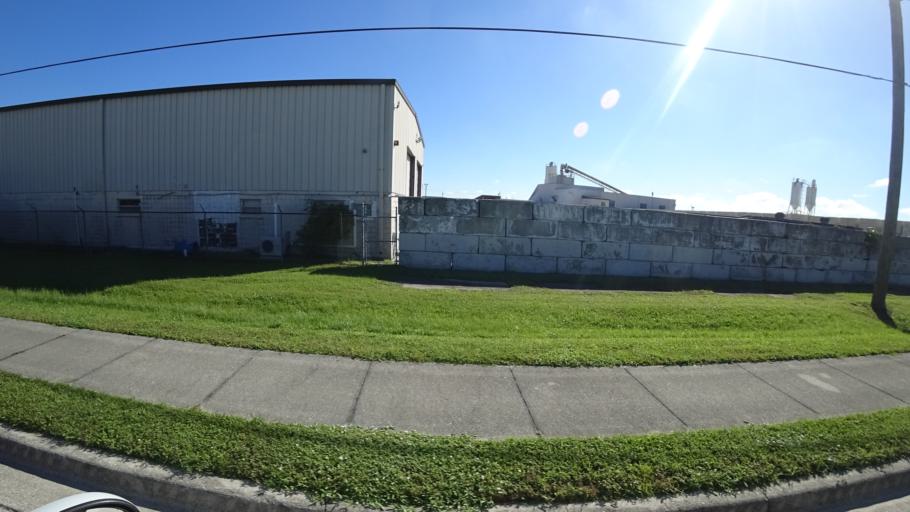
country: US
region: Florida
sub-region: Manatee County
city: West Samoset
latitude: 27.4824
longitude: -82.5547
